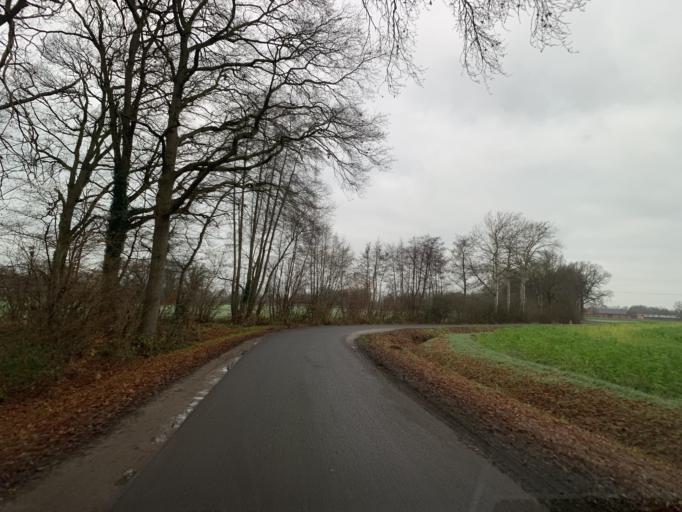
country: DE
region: North Rhine-Westphalia
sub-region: Regierungsbezirk Munster
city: Greven
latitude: 52.0708
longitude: 7.5441
